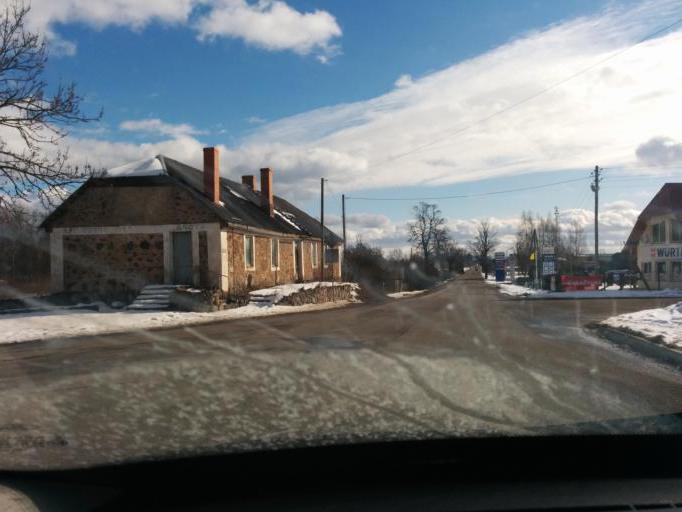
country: LV
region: Gulbenes Rajons
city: Gulbene
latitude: 57.1840
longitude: 26.7366
